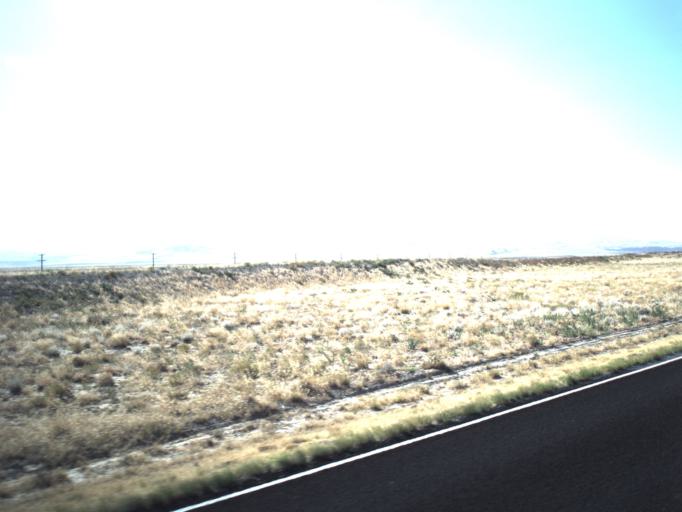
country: US
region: Utah
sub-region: Millard County
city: Fillmore
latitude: 38.9167
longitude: -112.8135
